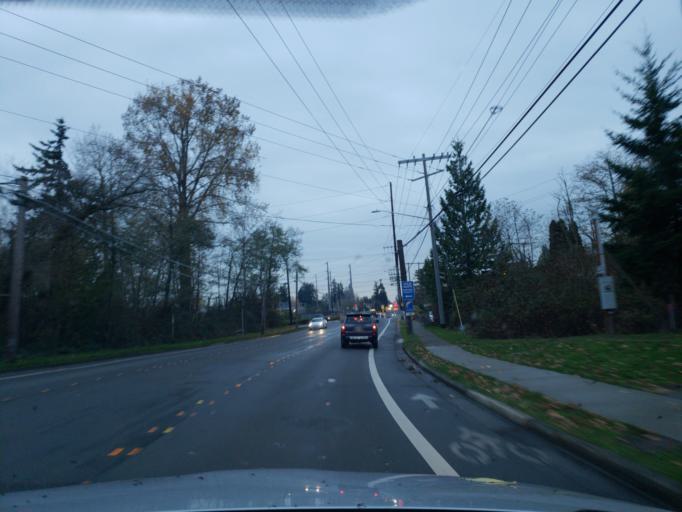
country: US
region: Washington
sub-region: Snohomish County
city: Lynnwood
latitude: 47.8067
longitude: -122.3144
